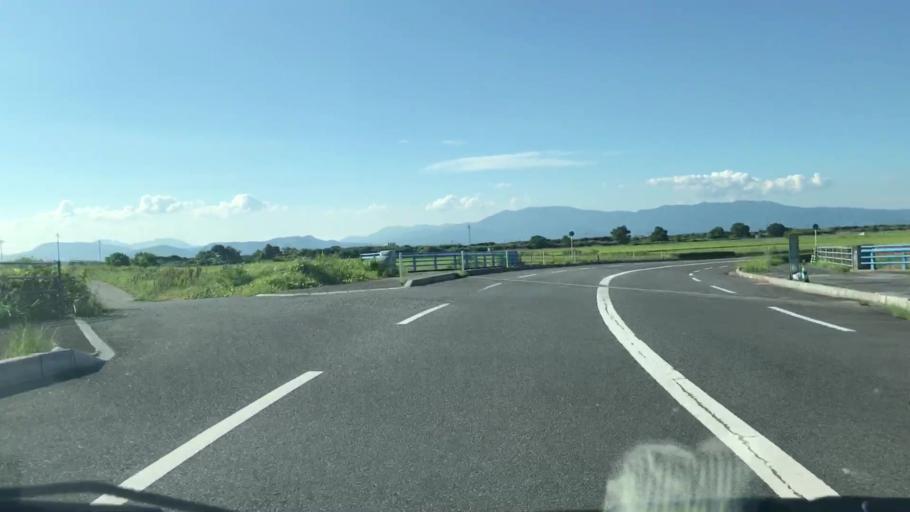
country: JP
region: Saga Prefecture
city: Okawa
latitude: 33.1601
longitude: 130.2904
